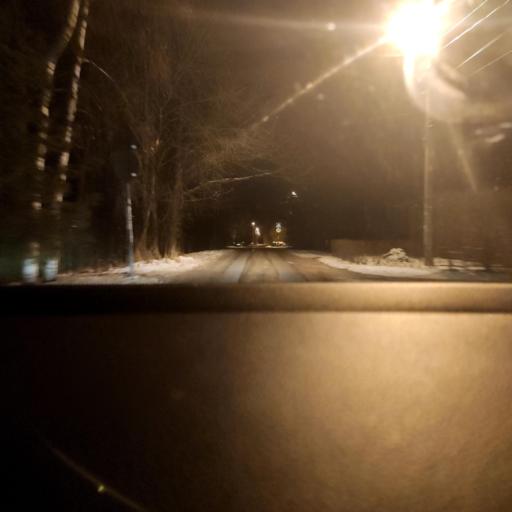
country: RU
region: Moskovskaya
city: Zhavoronki
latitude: 55.6368
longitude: 37.0857
